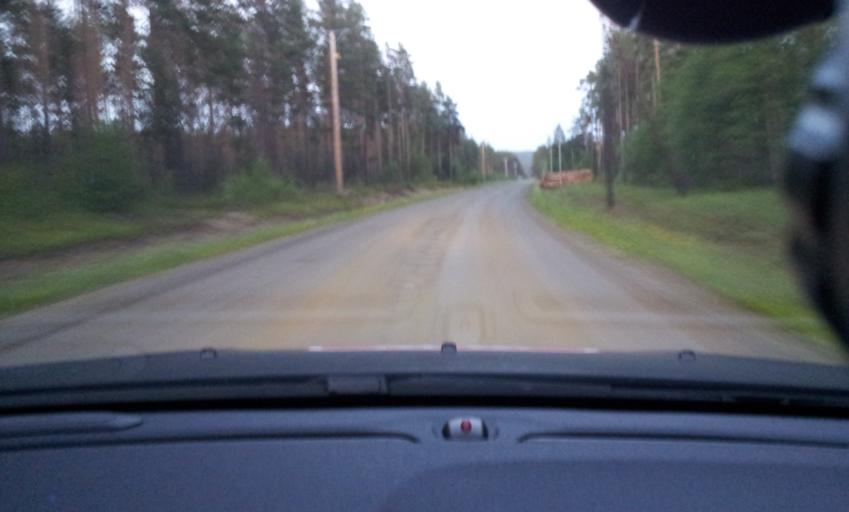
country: SE
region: Vaesternorrland
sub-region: Ange Kommun
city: Fransta
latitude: 62.7869
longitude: 16.0623
